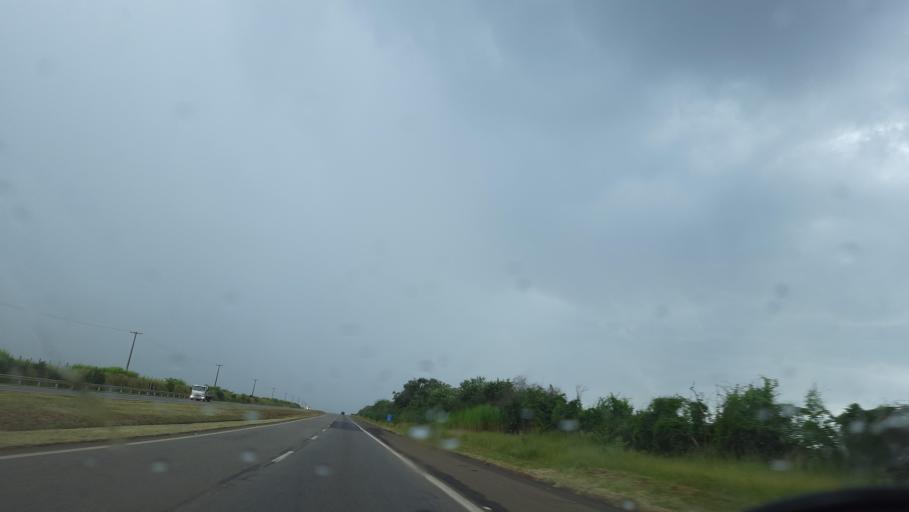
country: BR
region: Sao Paulo
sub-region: Aguai
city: Aguai
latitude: -22.1262
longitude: -47.0010
